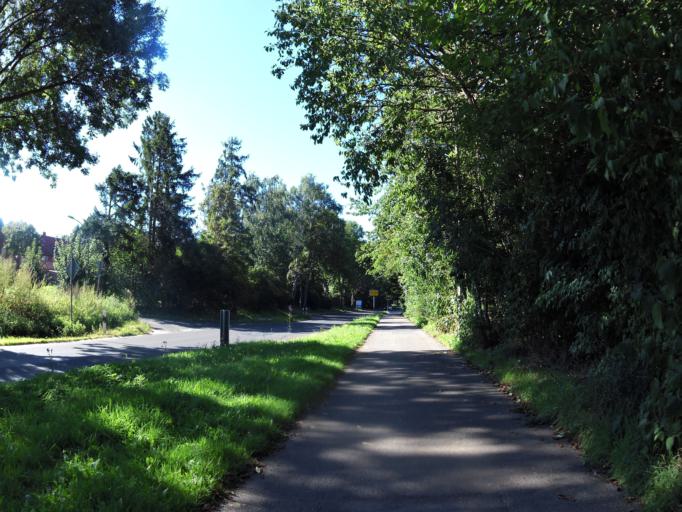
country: DE
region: North Rhine-Westphalia
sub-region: Regierungsbezirk Koln
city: Ubach-Palenberg
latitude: 50.9321
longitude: 6.1016
